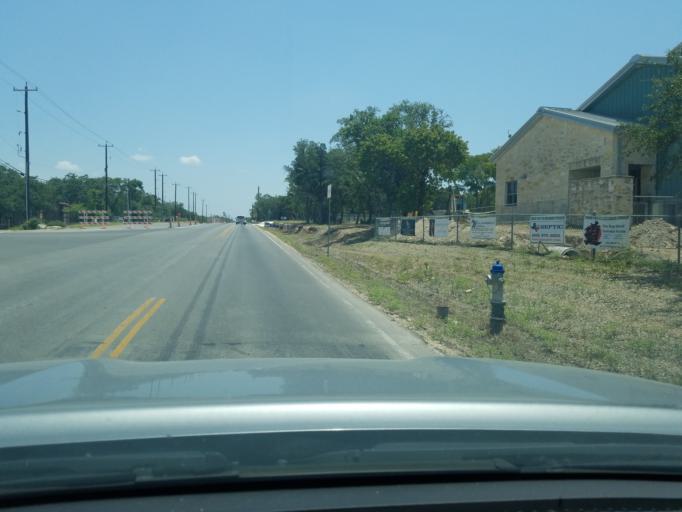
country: US
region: Texas
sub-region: Bexar County
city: Timberwood Park
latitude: 29.7081
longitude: -98.5112
